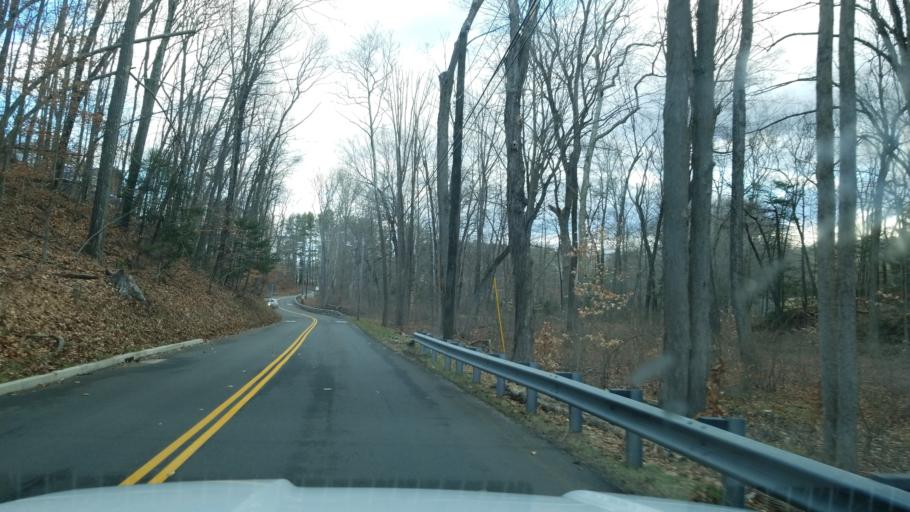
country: US
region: Connecticut
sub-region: Middlesex County
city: Durham
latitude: 41.5040
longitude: -72.6325
